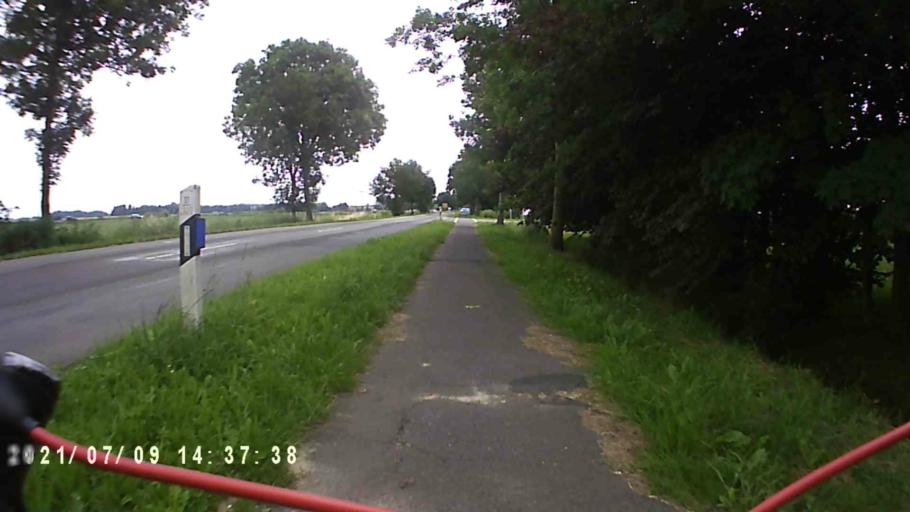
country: DE
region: Lower Saxony
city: Weener
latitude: 53.1142
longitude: 7.3424
